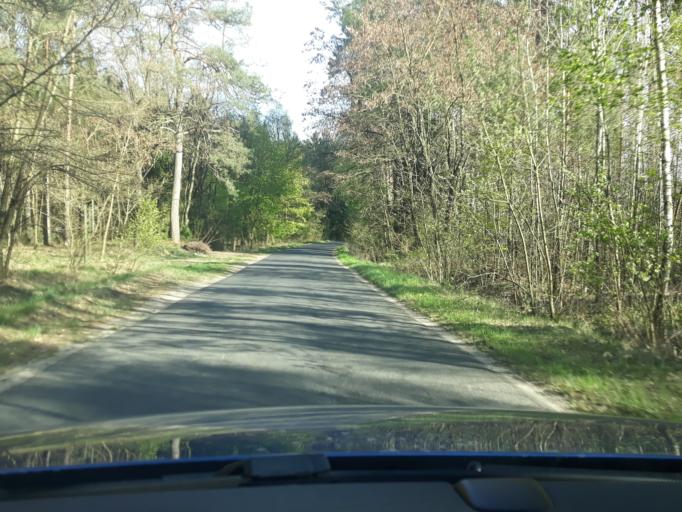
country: PL
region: Pomeranian Voivodeship
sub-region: Powiat czluchowski
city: Przechlewo
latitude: 53.8589
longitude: 17.3466
